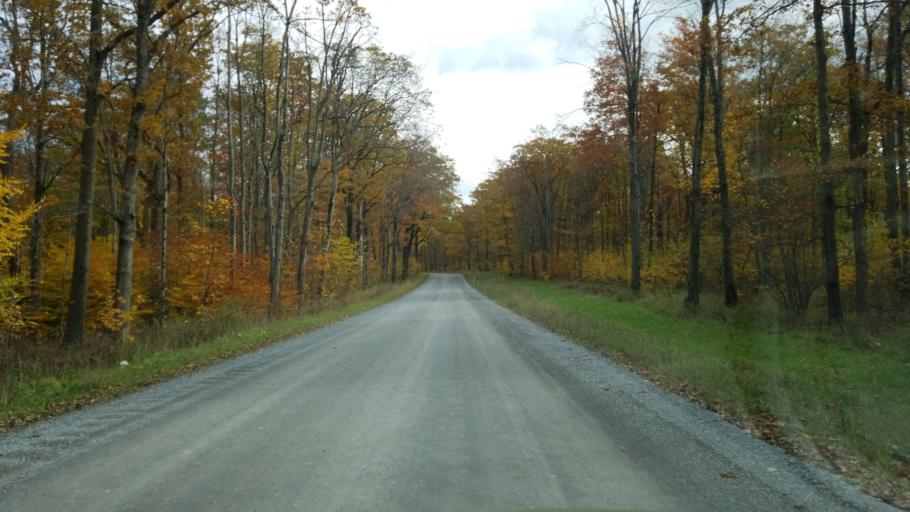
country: US
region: Pennsylvania
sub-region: Clearfield County
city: Clearfield
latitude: 41.1388
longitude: -78.5099
